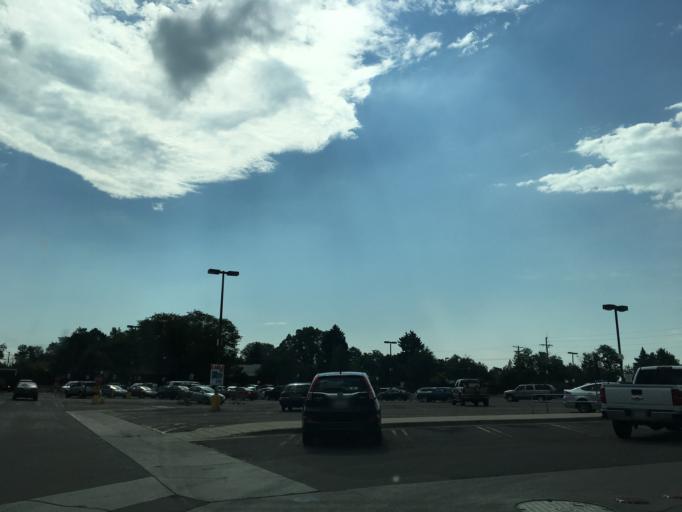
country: US
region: Colorado
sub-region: Jefferson County
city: Lakewood
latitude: 39.6905
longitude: -105.0528
